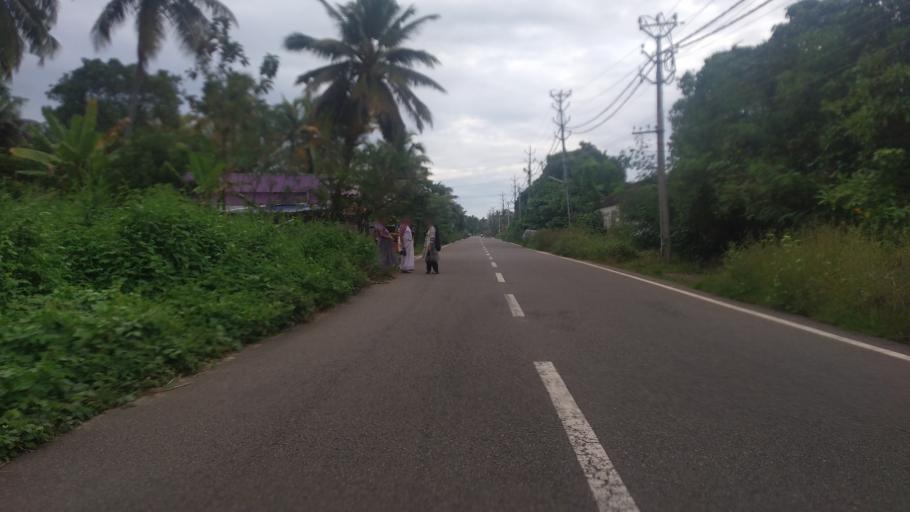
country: IN
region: Kerala
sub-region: Ernakulam
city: Cochin
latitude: 9.8596
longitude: 76.2691
